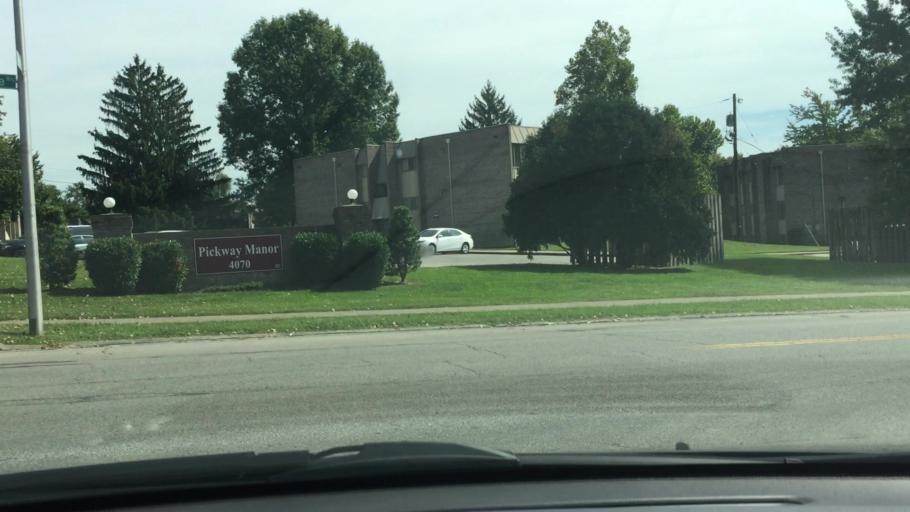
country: US
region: Kentucky
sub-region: Fayette County
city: Monticello
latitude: 37.9711
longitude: -84.5248
